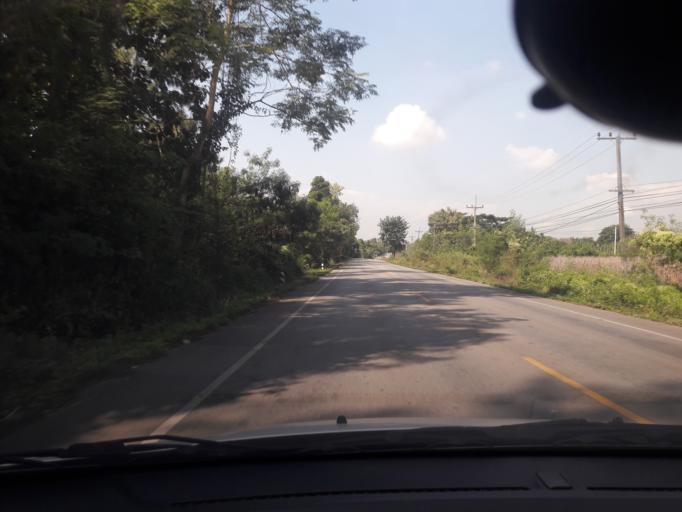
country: TH
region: Lampang
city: Mae Tha
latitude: 18.1921
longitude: 99.5224
